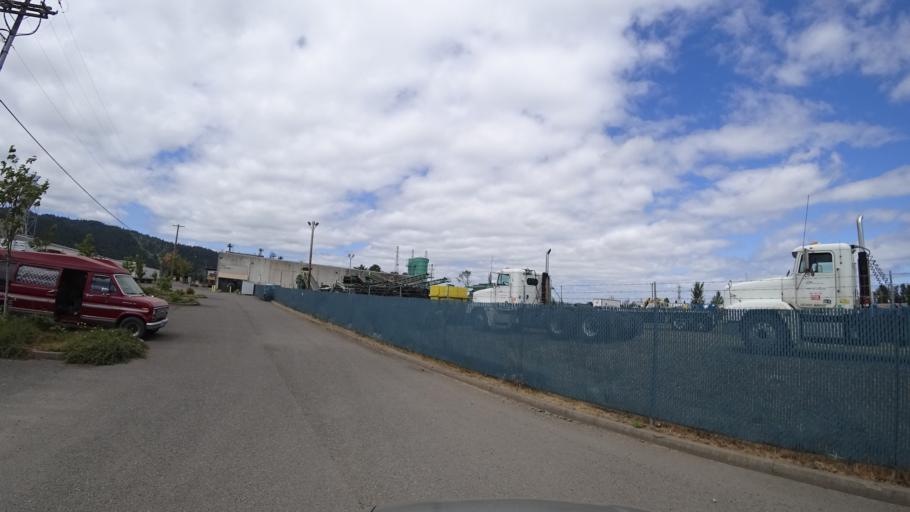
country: US
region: Oregon
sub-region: Washington County
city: Cedar Mill
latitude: 45.6131
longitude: -122.7768
